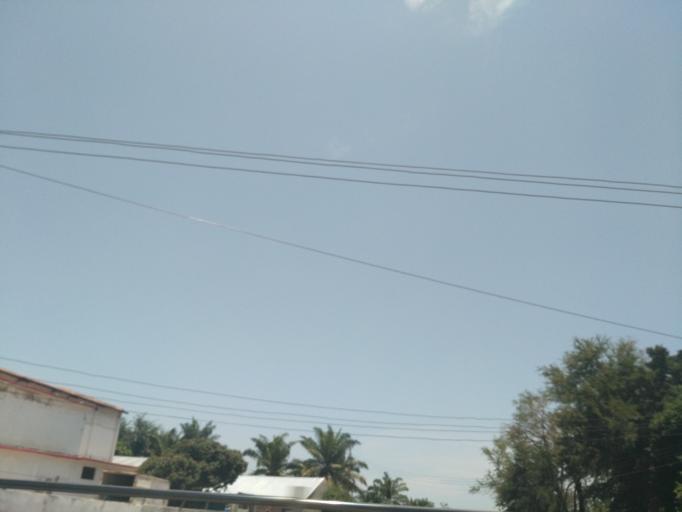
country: TZ
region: Mwanza
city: Mwanza
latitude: -2.5157
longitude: 32.8986
